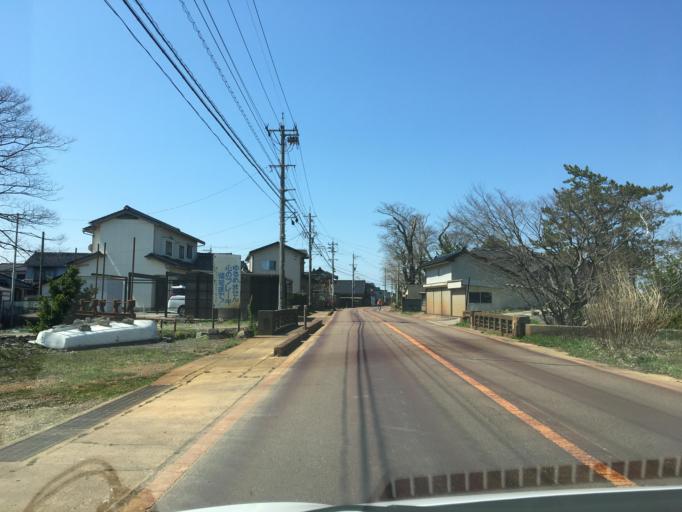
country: JP
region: Toyama
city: Kuragaki-kosugi
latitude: 36.7567
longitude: 137.1880
